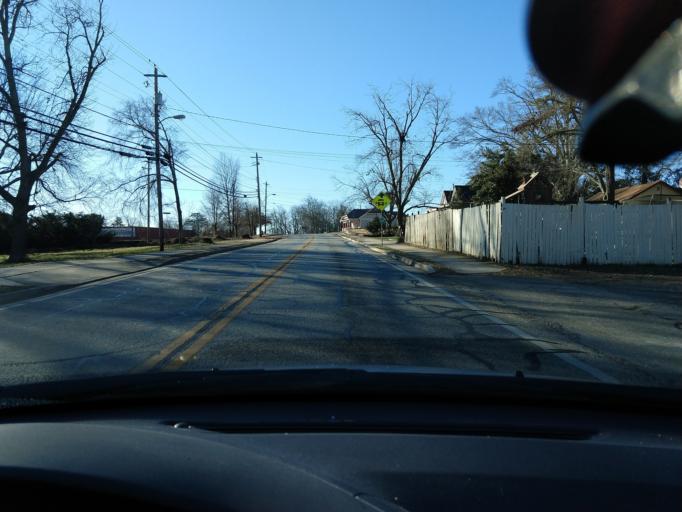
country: US
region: Georgia
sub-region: Jackson County
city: Commerce
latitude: 34.2102
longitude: -83.4625
